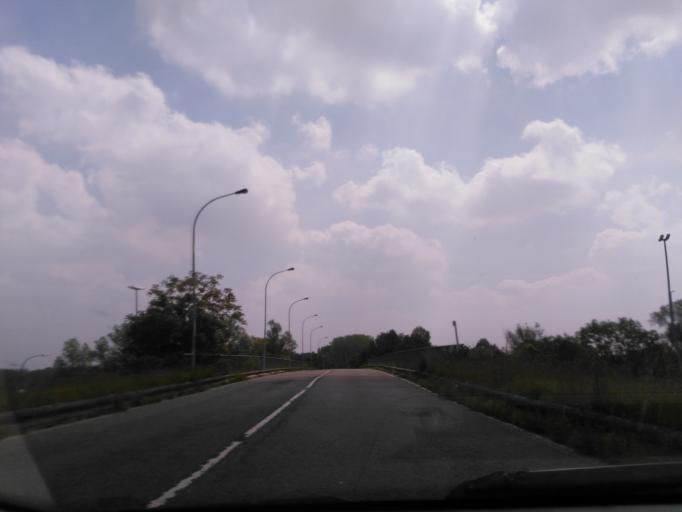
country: BE
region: Flanders
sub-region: Provincie Oost-Vlaanderen
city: Kruibeke
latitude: 51.1818
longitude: 4.2806
